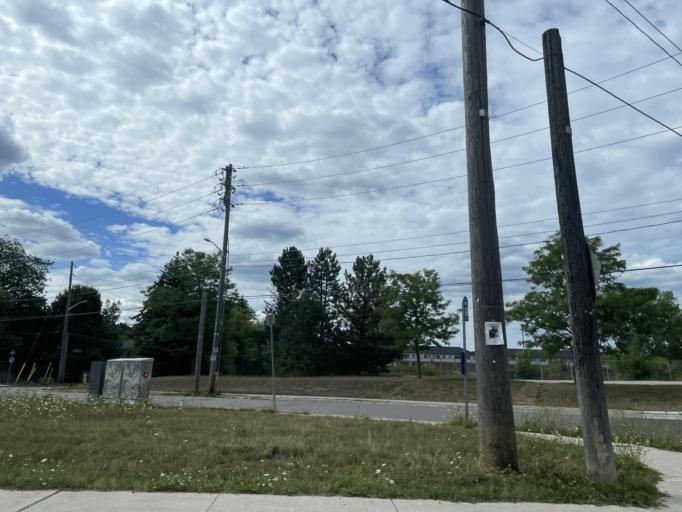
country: CA
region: Ontario
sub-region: Wellington County
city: Guelph
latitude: 43.5455
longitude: -80.2327
